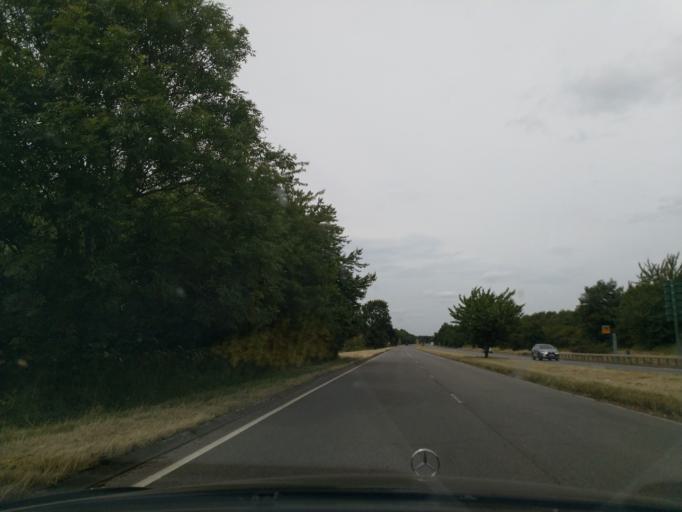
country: GB
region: England
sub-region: Solihull
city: Barston
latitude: 52.4144
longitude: -1.6751
